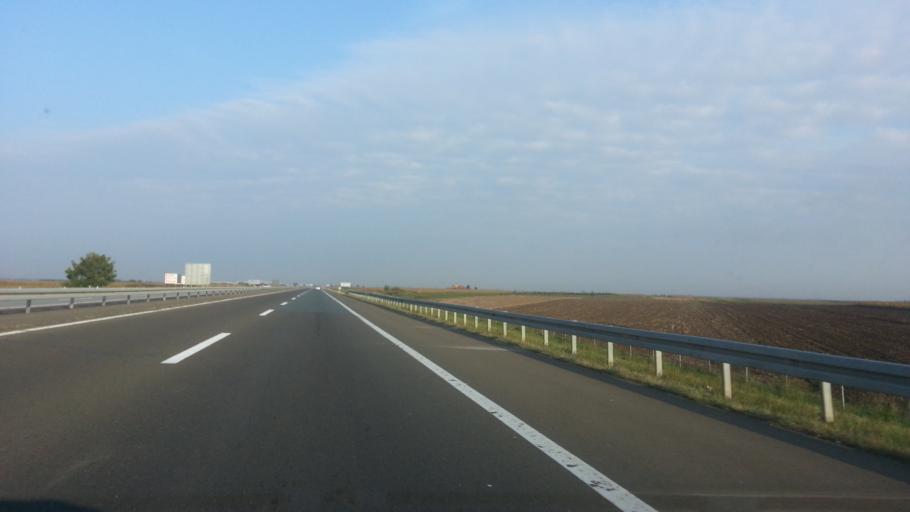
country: RS
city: Novi Banovci
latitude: 44.9501
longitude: 20.2698
